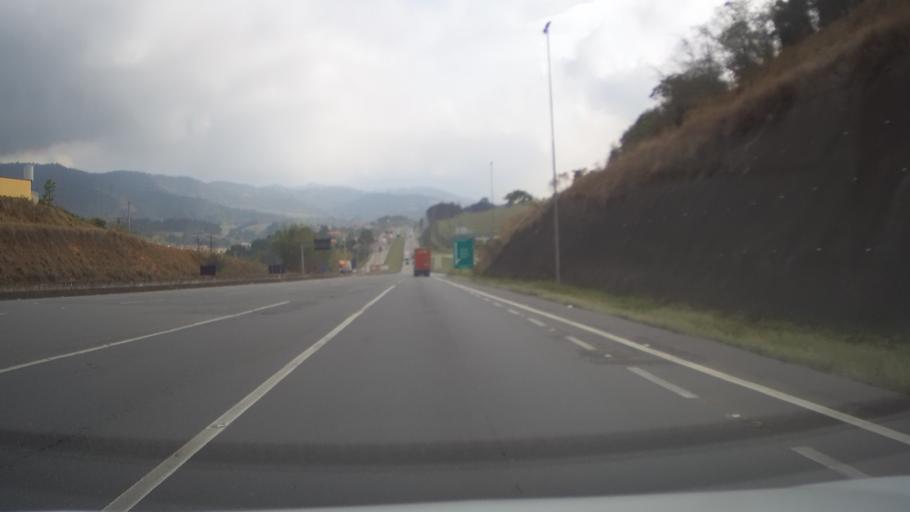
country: BR
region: Minas Gerais
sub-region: Extrema
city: Extrema
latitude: -22.9073
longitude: -46.4235
